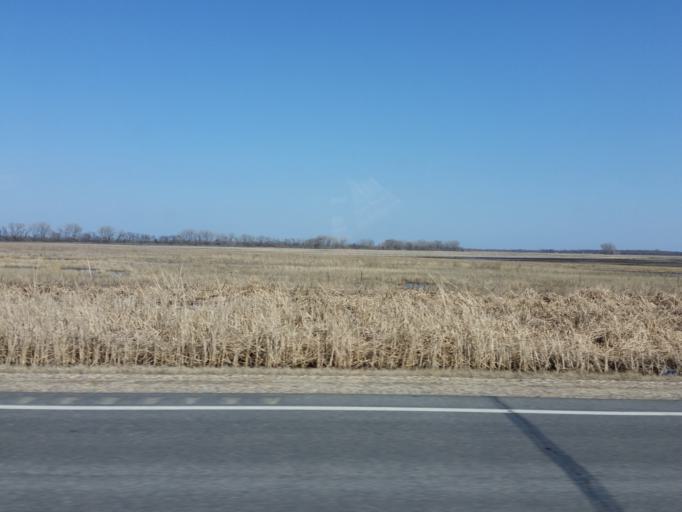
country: US
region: North Dakota
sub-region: Grand Forks County
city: Grand Forks Air Force Base
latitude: 48.1091
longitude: -97.2153
